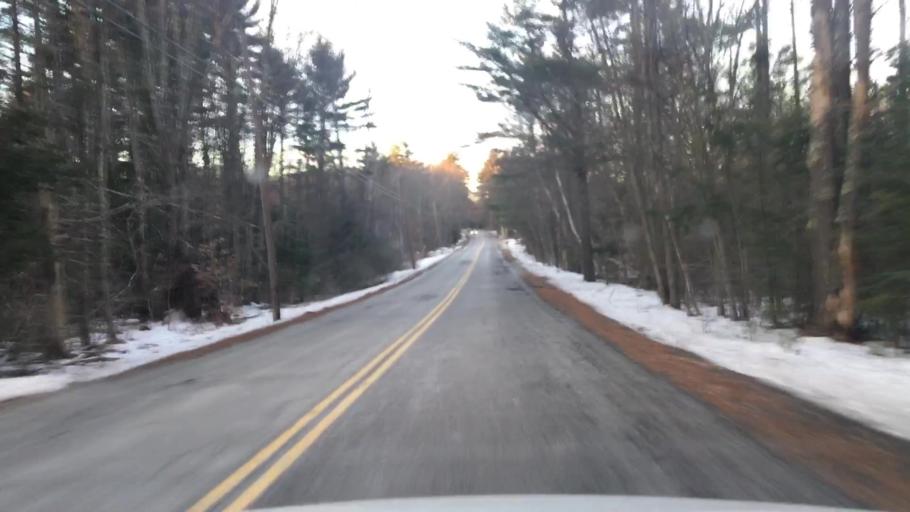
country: US
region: Maine
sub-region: York County
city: Lebanon
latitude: 43.3312
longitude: -70.8641
